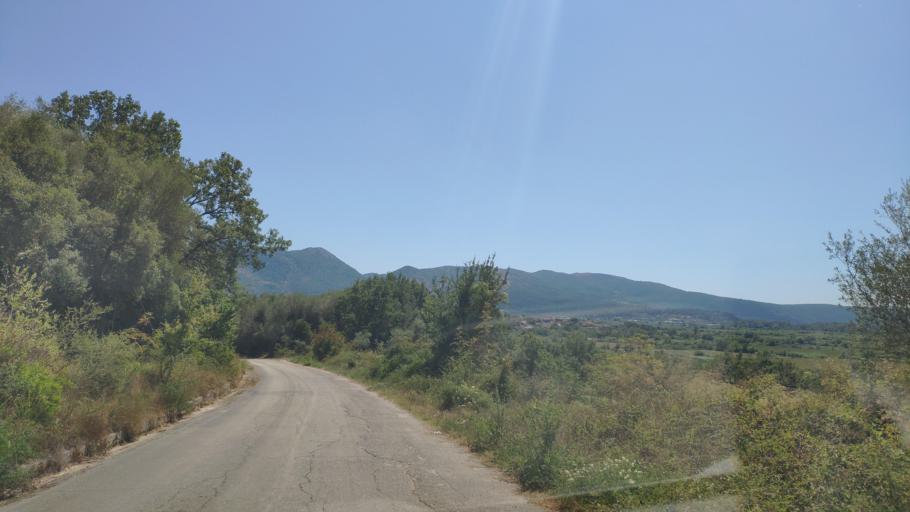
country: GR
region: Epirus
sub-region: Nomos Prevezis
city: Kanalaki
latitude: 39.2698
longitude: 20.6005
